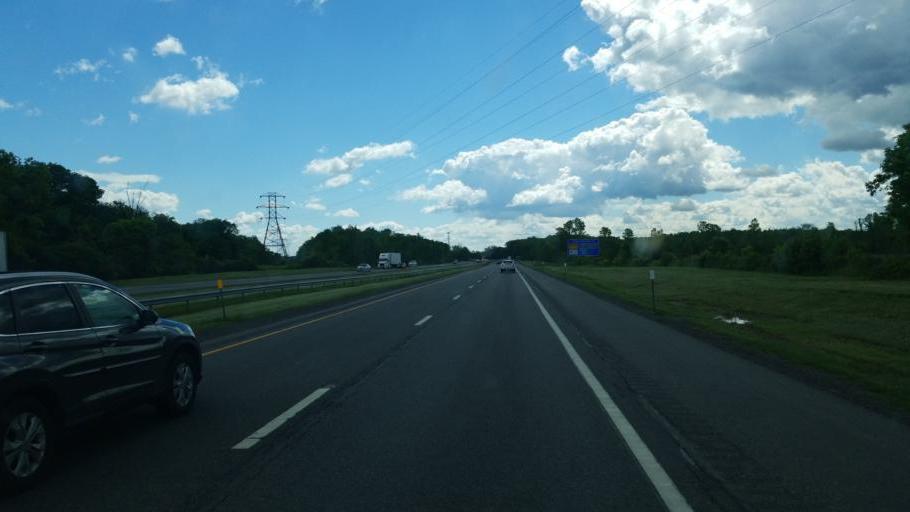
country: US
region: New York
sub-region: Madison County
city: Canastota
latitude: 43.0909
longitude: -75.7736
